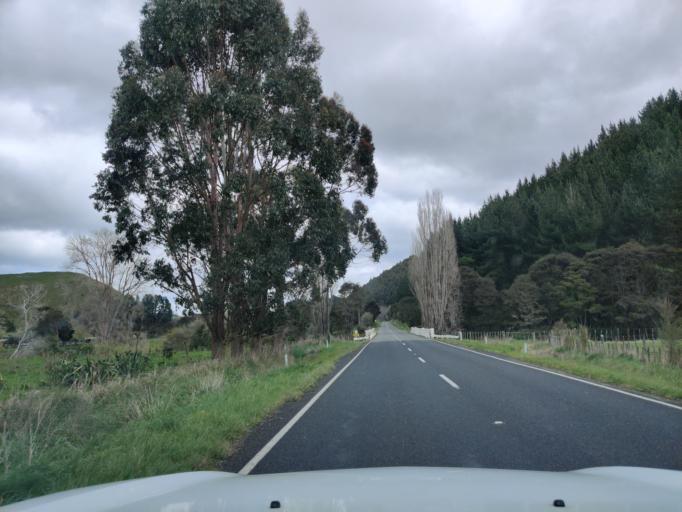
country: NZ
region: Manawatu-Wanganui
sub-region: Wanganui District
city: Wanganui
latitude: -39.8325
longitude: 175.1659
